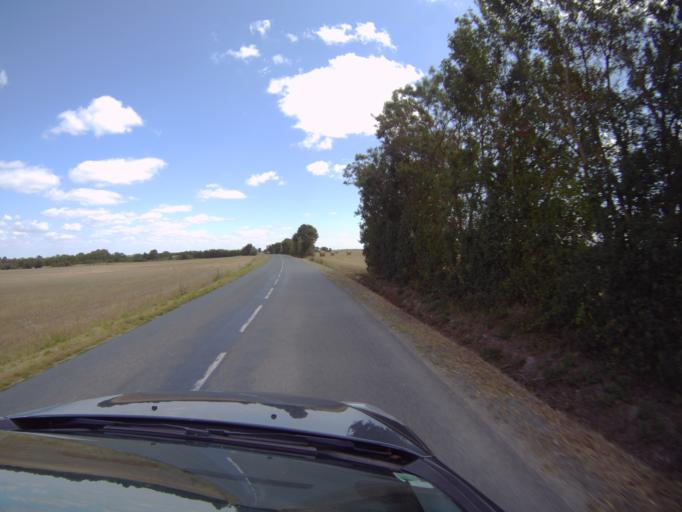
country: FR
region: Poitou-Charentes
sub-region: Departement de la Charente-Maritime
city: Saint-Jean-de-Liversay
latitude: 46.2621
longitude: -0.8695
